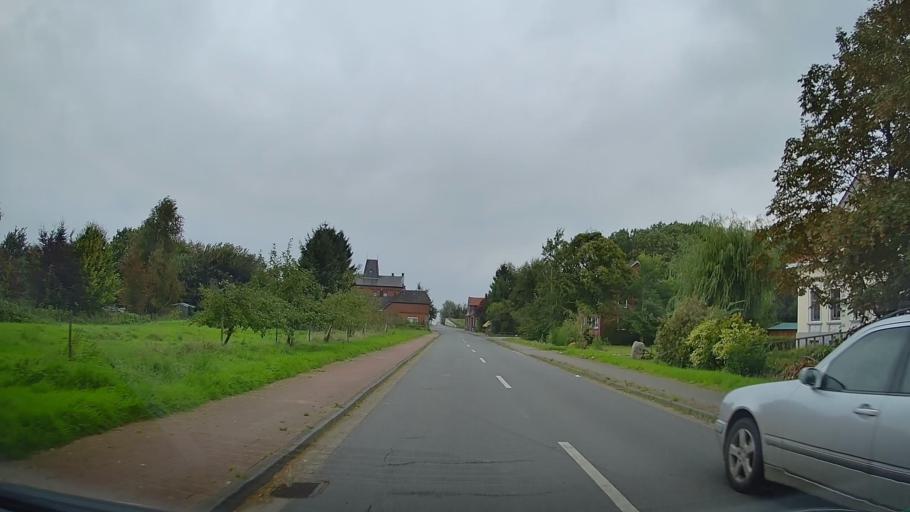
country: DE
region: Lower Saxony
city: Balje
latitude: 53.8304
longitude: 9.1335
